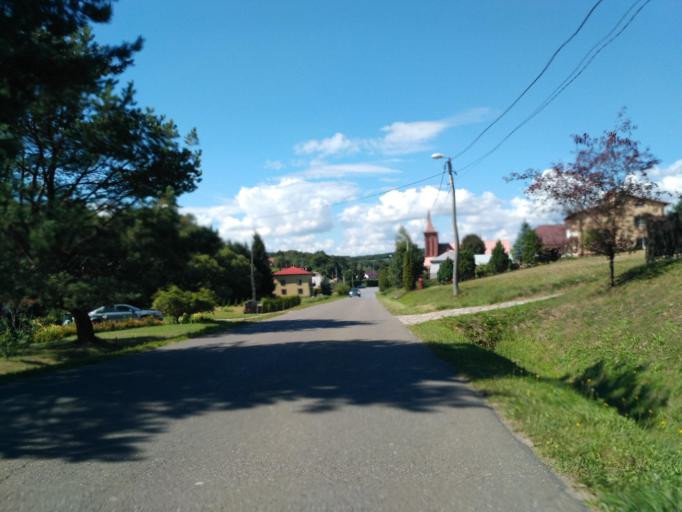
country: PL
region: Subcarpathian Voivodeship
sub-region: Powiat jasielski
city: Skolyszyn
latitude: 49.7916
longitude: 21.3380
